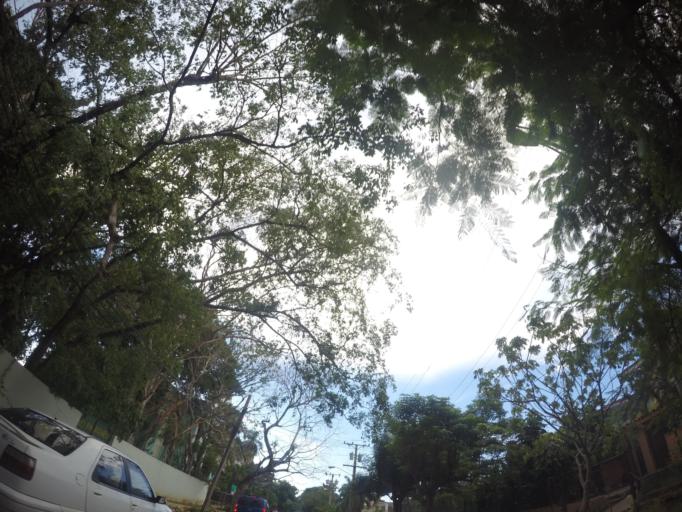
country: CU
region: La Habana
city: Havana
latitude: 23.1192
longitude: -82.4231
